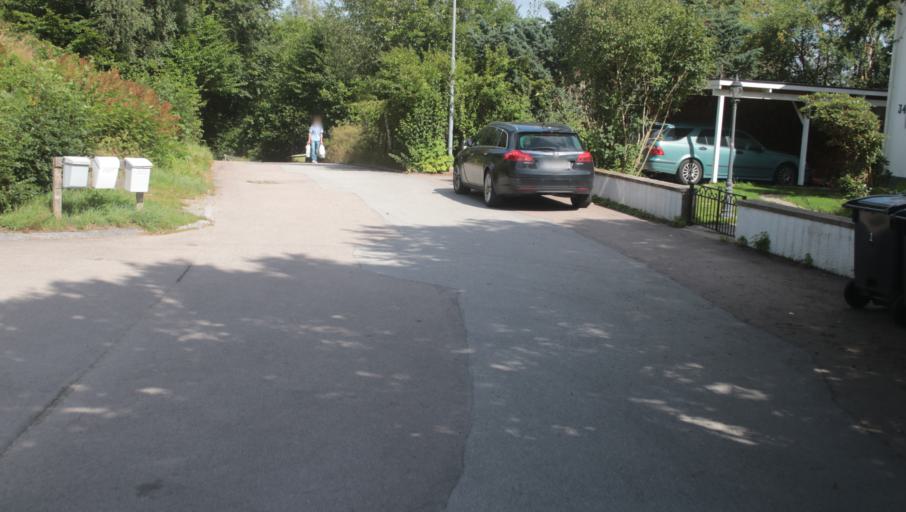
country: SE
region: Blekinge
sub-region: Karlshamns Kommun
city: Svangsta
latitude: 56.2621
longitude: 14.7661
